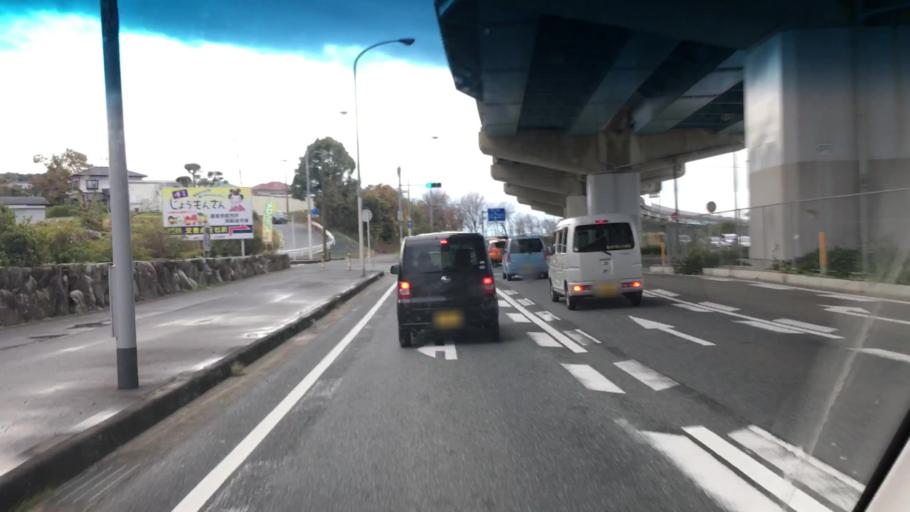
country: JP
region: Fukuoka
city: Maebaru-chuo
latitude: 33.5683
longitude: 130.2476
